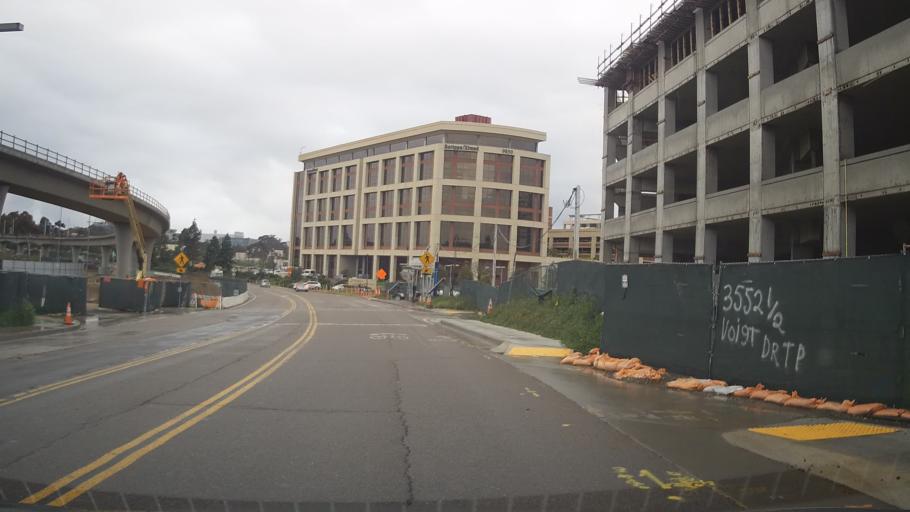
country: US
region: California
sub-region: San Diego County
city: La Jolla
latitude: 32.8823
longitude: -117.2243
